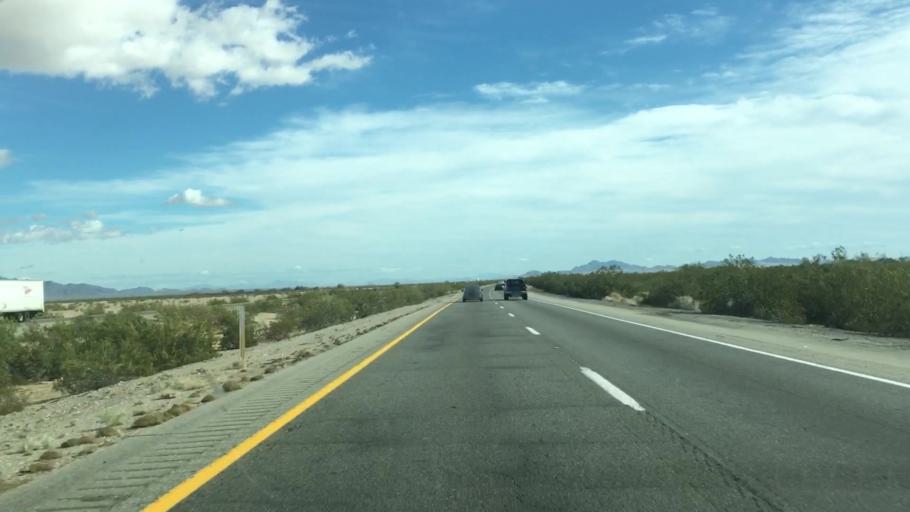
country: US
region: California
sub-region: Riverside County
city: Mesa Verde
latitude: 33.6207
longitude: -115.0355
